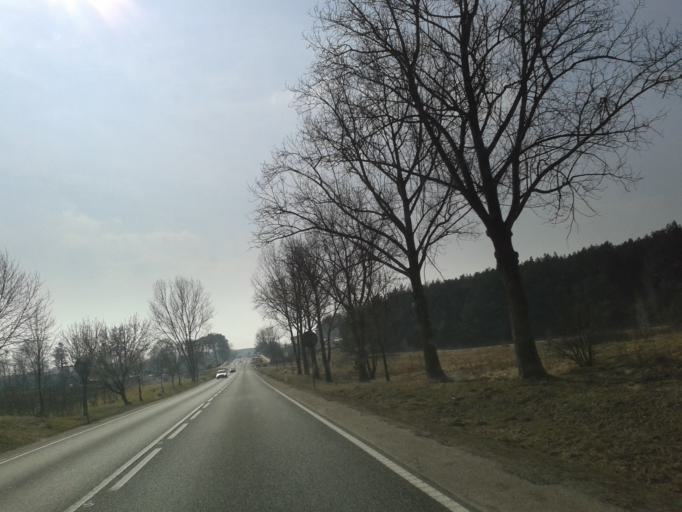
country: PL
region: Pomeranian Voivodeship
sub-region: Powiat czluchowski
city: Debrzno
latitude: 53.5861
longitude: 17.1169
